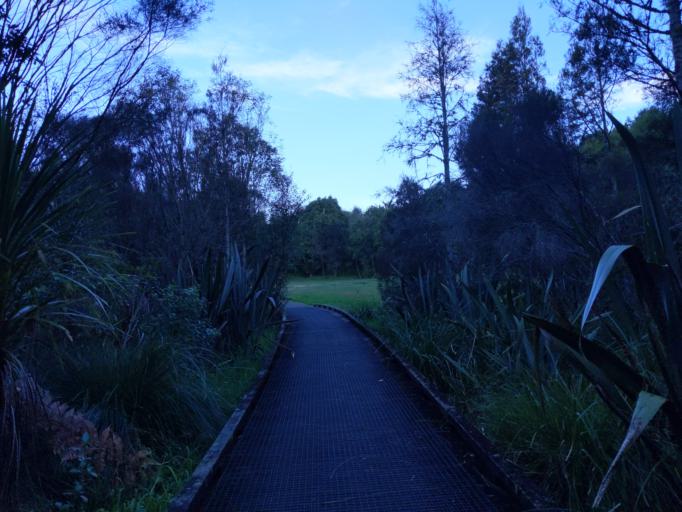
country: NZ
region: Waikato
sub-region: Hamilton City
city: Hamilton
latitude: -37.7435
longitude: 175.2756
